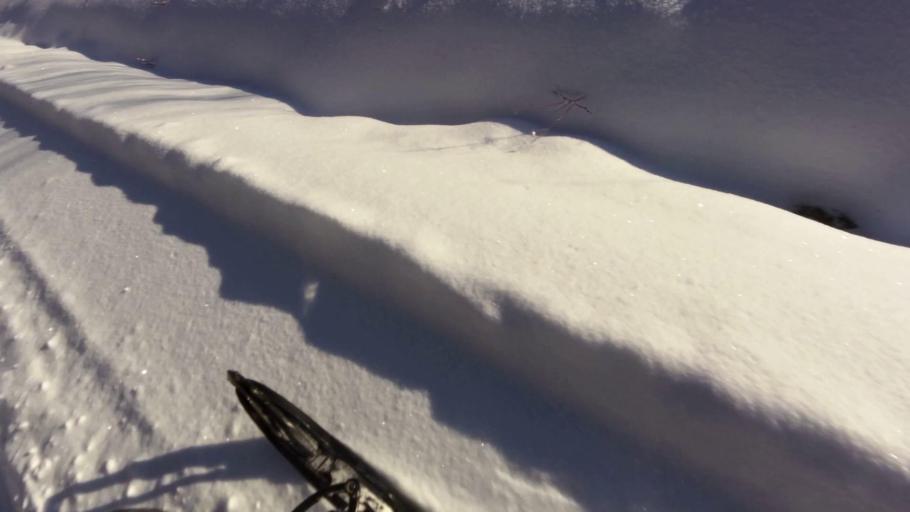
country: US
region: New York
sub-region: Chautauqua County
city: Falconer
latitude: 42.2353
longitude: -79.2177
